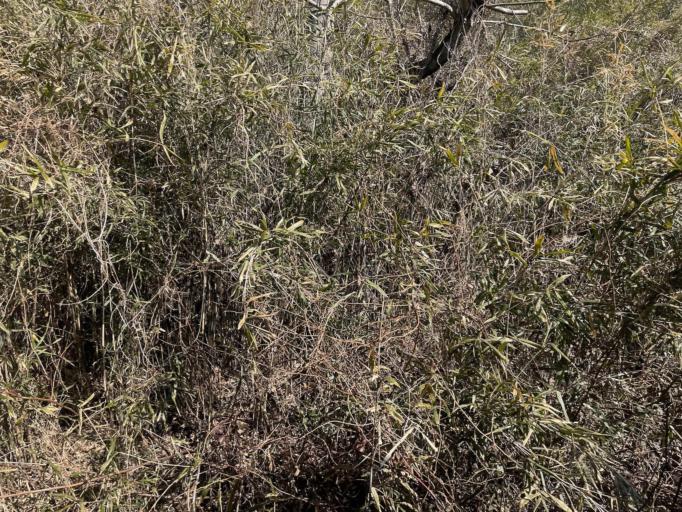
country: JP
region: Gunma
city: Nakanojomachi
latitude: 36.5526
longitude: 138.7850
